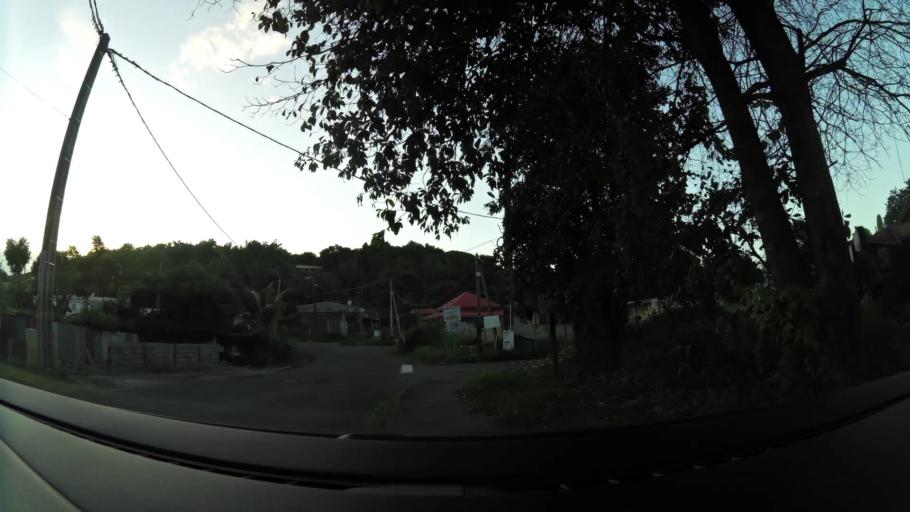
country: GP
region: Guadeloupe
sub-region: Guadeloupe
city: Les Abymes
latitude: 16.2702
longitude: -61.4978
